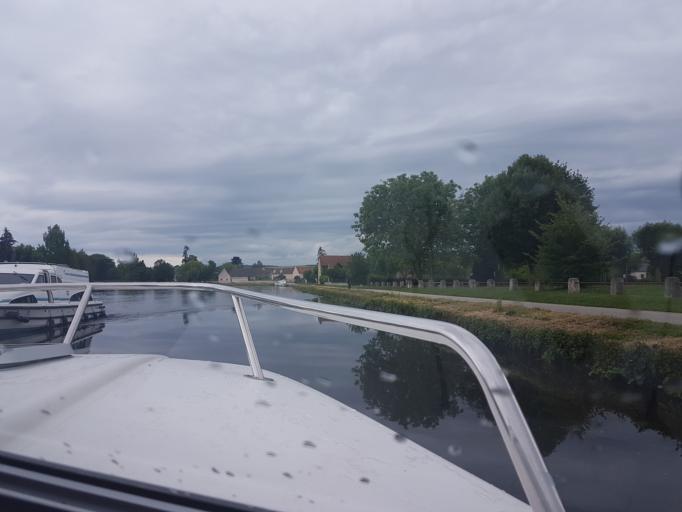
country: FR
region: Bourgogne
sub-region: Departement de l'Yonne
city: Saint-Bris-le-Vineux
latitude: 47.7041
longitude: 3.6363
